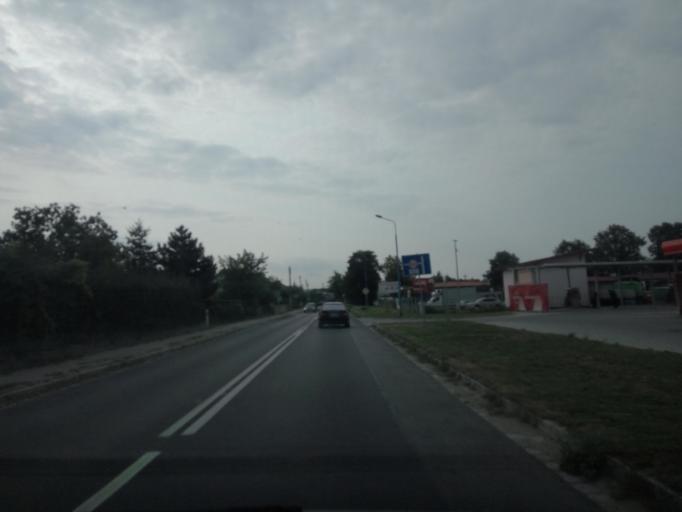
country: PL
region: Lower Silesian Voivodeship
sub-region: Powiat strzelinski
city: Strzelin
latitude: 50.7912
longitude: 17.0661
